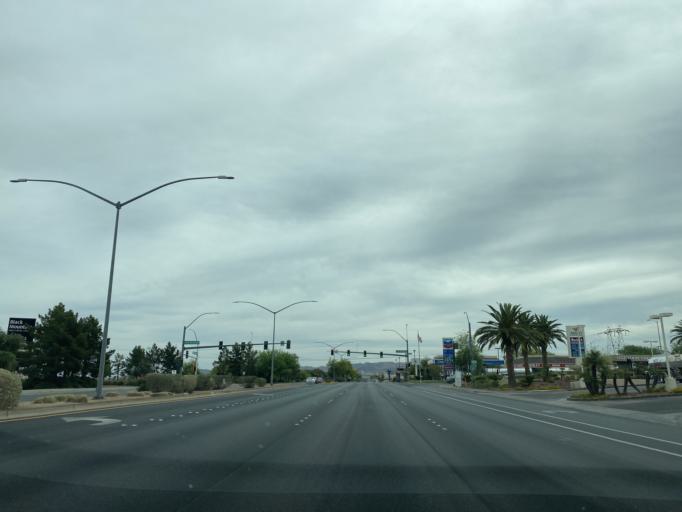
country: US
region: Nevada
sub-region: Clark County
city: Henderson
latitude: 36.0351
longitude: -115.0016
